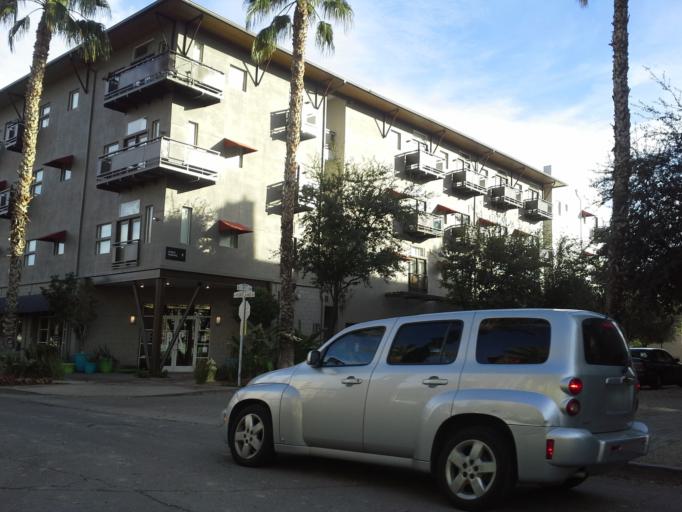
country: US
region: Arizona
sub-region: Maricopa County
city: Phoenix
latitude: 33.4599
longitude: -112.0755
